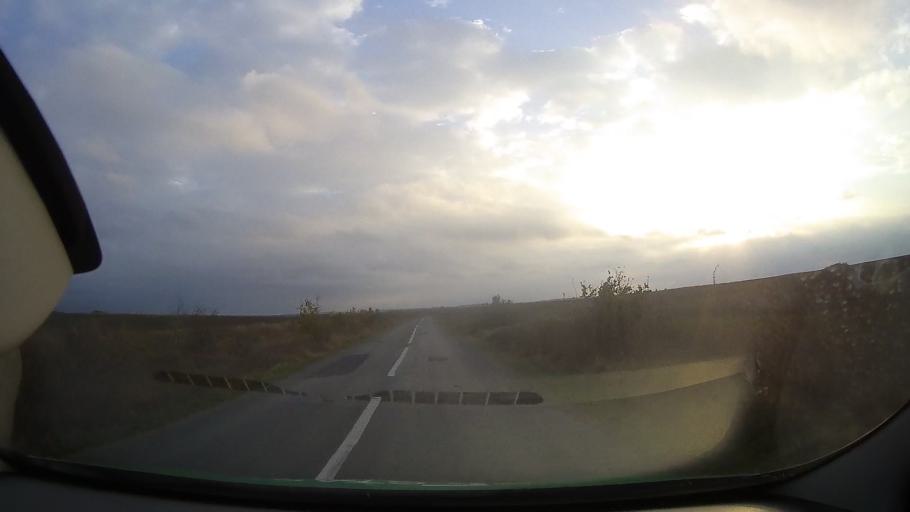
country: RO
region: Constanta
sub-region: Comuna Adamclisi
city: Adamclisi
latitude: 44.0207
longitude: 27.9067
